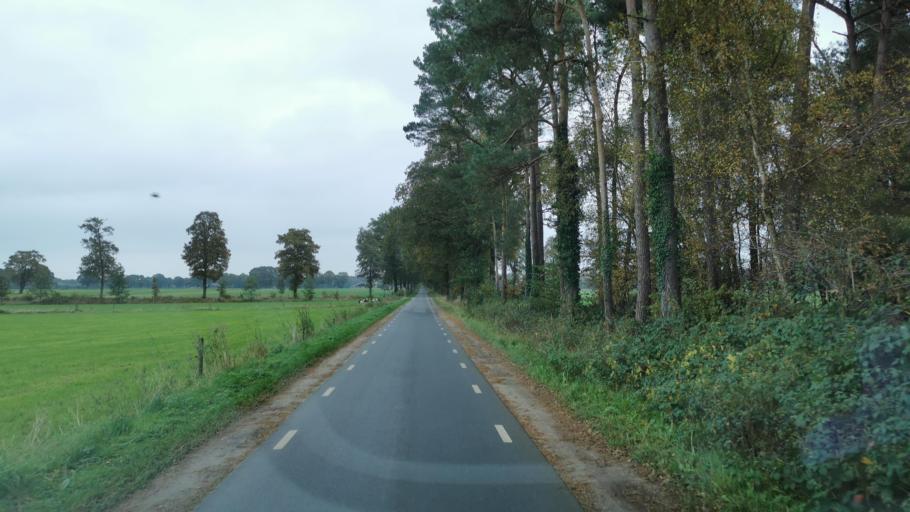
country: NL
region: Overijssel
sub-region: Gemeente Losser
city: Losser
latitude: 52.2432
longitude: 6.9822
